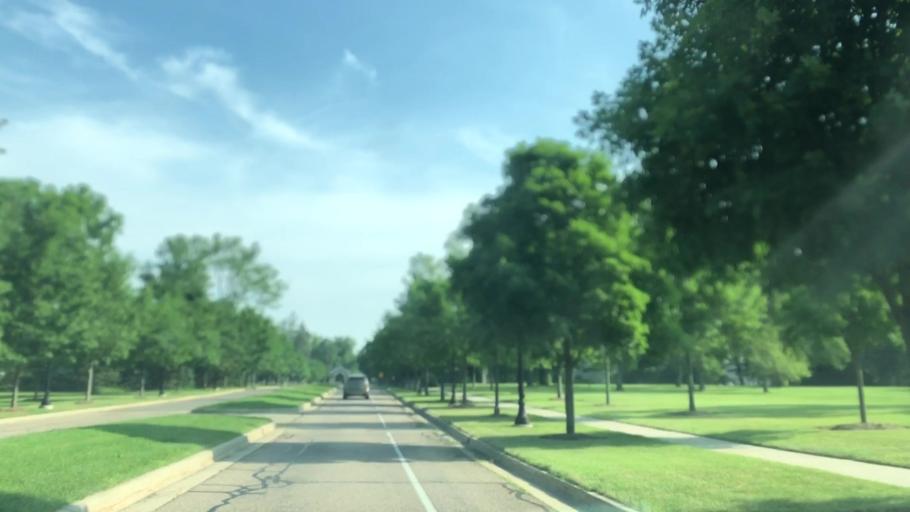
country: US
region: Michigan
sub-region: Berrien County
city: Berrien Springs
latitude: 41.9580
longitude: -86.3587
